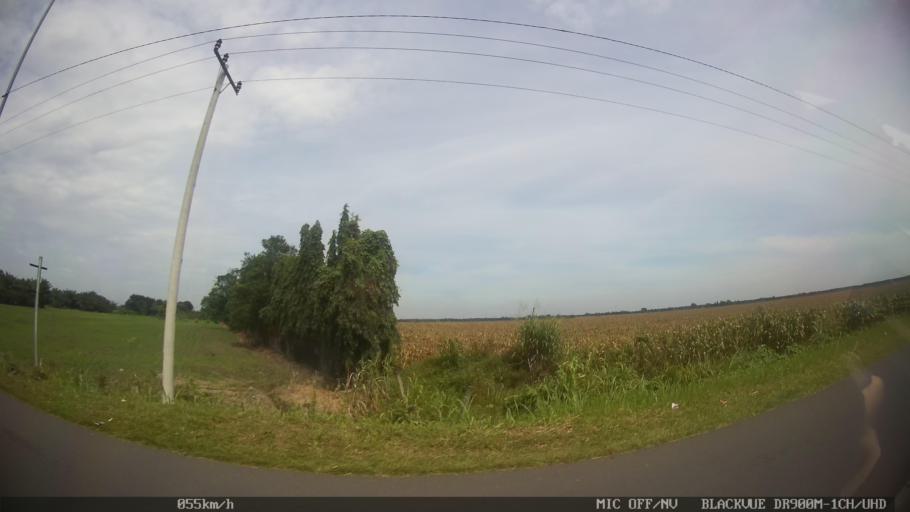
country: ID
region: North Sumatra
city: Sunggal
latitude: 3.6254
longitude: 98.6287
